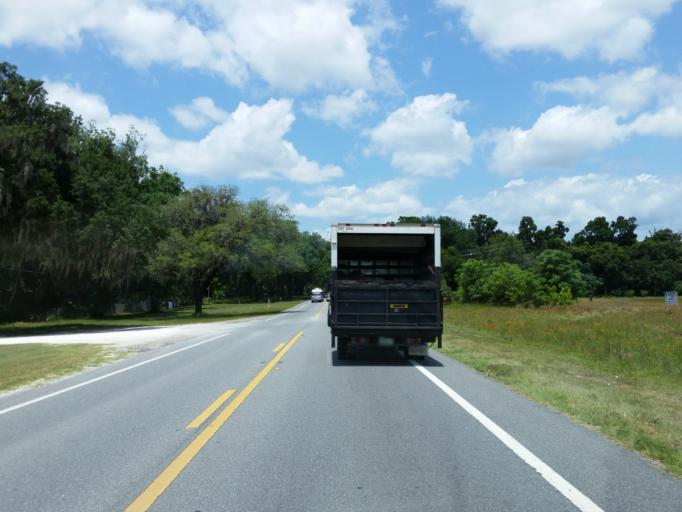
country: US
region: Florida
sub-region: Marion County
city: Belleview
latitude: 29.0019
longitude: -82.0413
